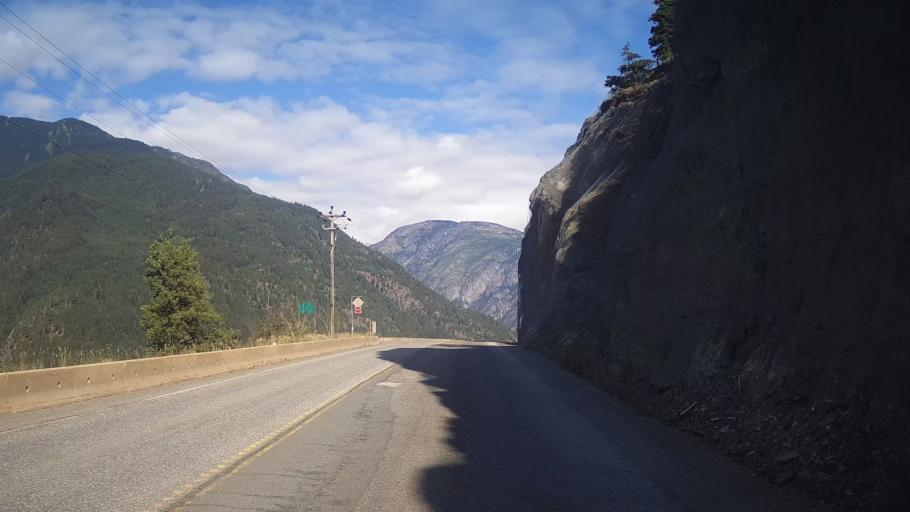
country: CA
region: British Columbia
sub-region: Thompson-Nicola Regional District
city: Ashcroft
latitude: 50.0769
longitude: -121.5487
